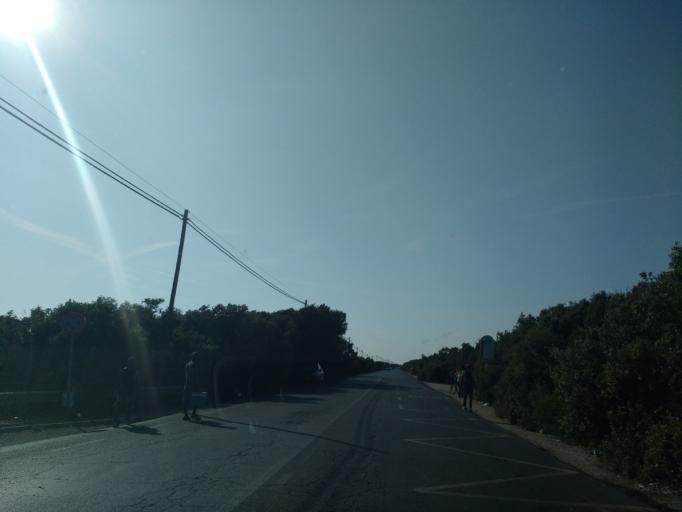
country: IT
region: Latium
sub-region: Citta metropolitana di Roma Capitale
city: Torvaianica
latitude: 41.6803
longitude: 12.3846
